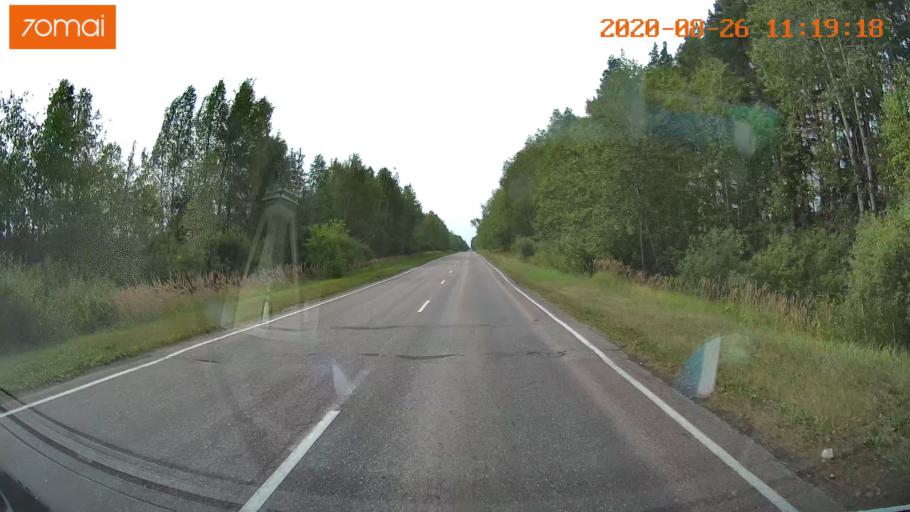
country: RU
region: Rjazan
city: Shilovo
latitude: 54.4007
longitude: 41.0821
